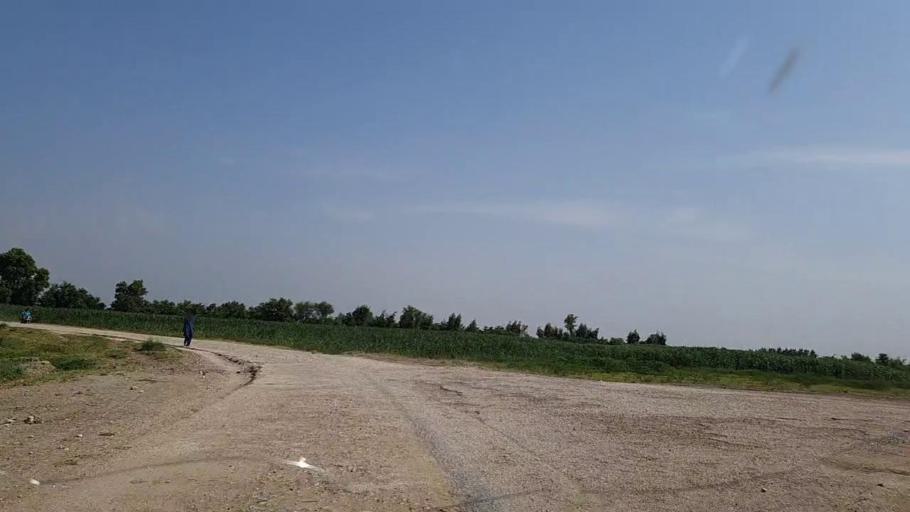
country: PK
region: Sindh
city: Khanpur
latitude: 27.7380
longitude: 69.3425
